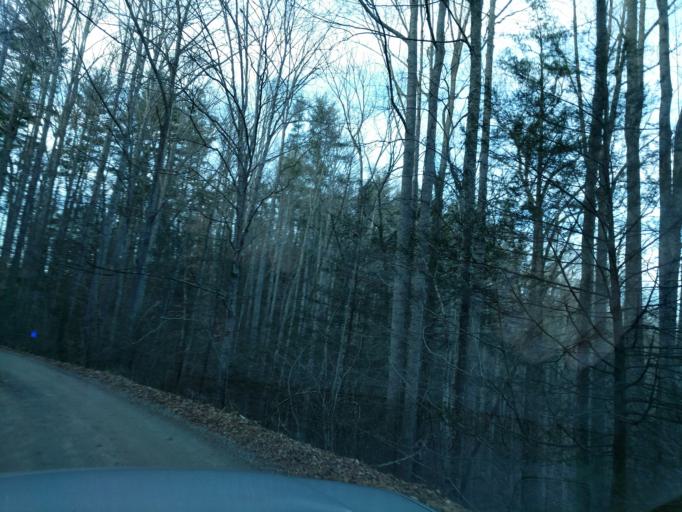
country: US
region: North Carolina
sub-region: Haywood County
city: Cove Creek
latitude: 35.7343
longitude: -83.0275
